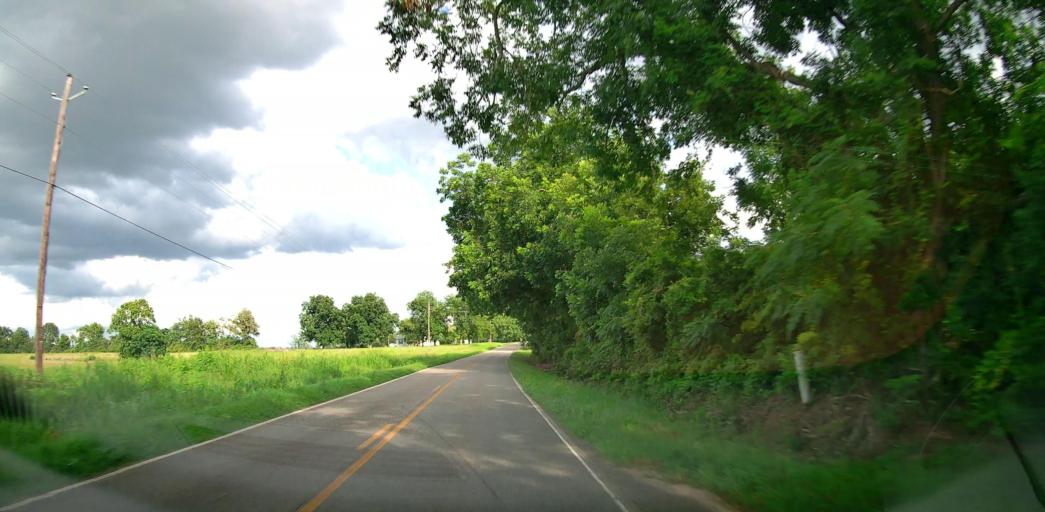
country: US
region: Georgia
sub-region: Bleckley County
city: Cochran
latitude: 32.4063
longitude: -83.3826
